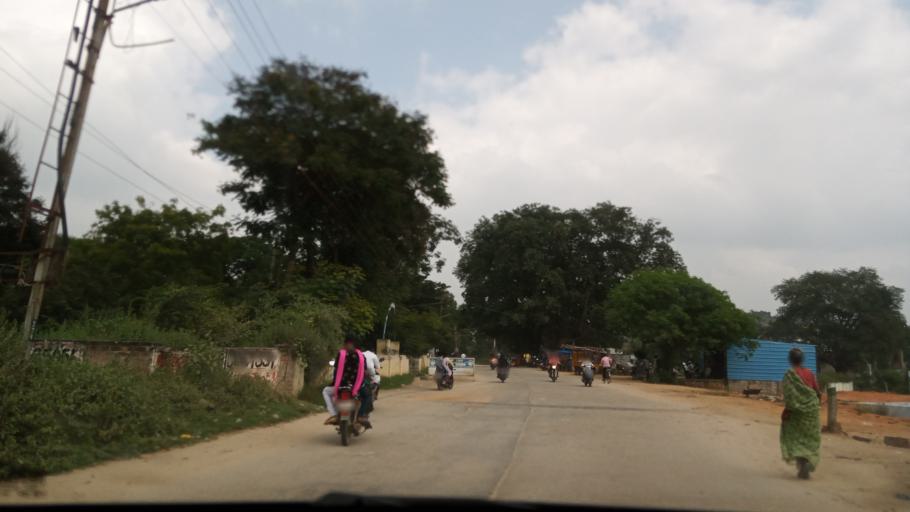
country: IN
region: Andhra Pradesh
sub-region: Chittoor
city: Madanapalle
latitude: 13.6390
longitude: 78.6326
